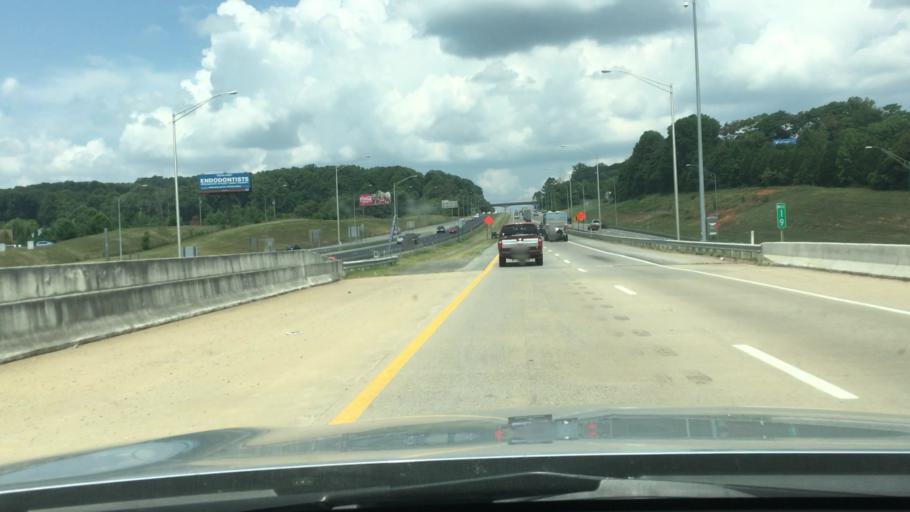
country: US
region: Tennessee
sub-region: Washington County
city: Johnson City
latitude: 36.3555
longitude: -82.3971
